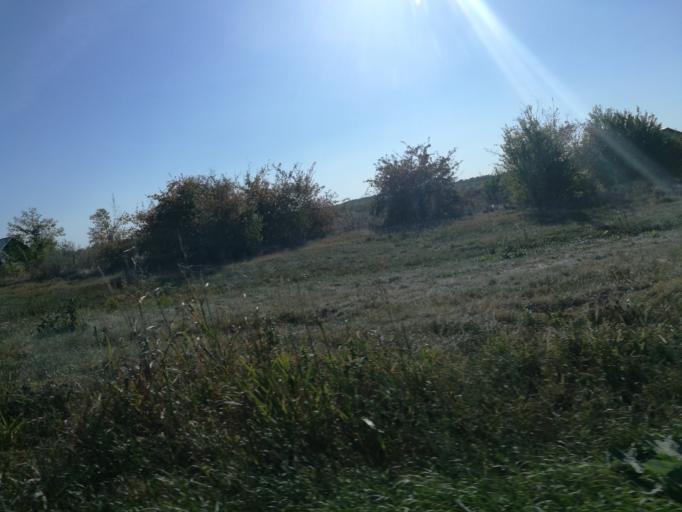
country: RO
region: Ilfov
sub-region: Comuna Dragomiresti-Vale
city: Dragomiresti-Vale
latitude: 44.4680
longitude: 25.9227
